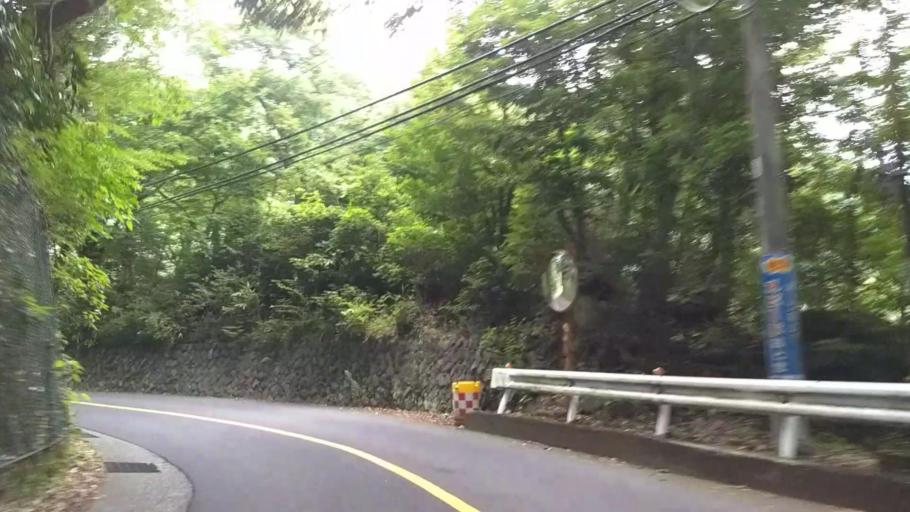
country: JP
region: Kanagawa
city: Odawara
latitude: 35.2270
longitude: 139.0944
